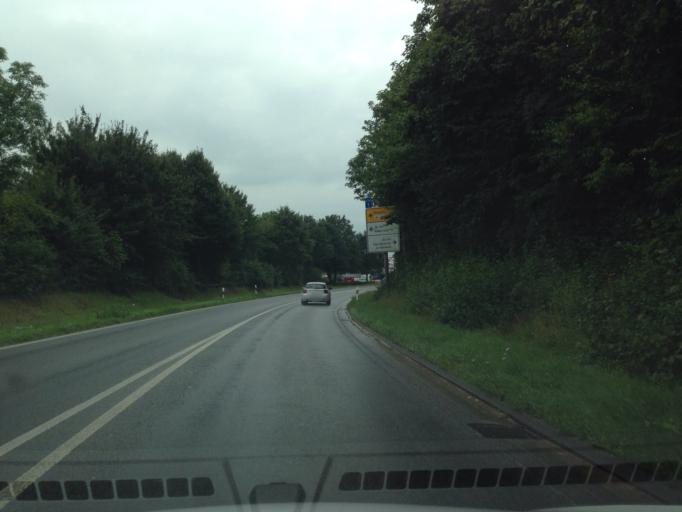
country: DE
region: North Rhine-Westphalia
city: Erkelenz
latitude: 51.0754
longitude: 6.3309
